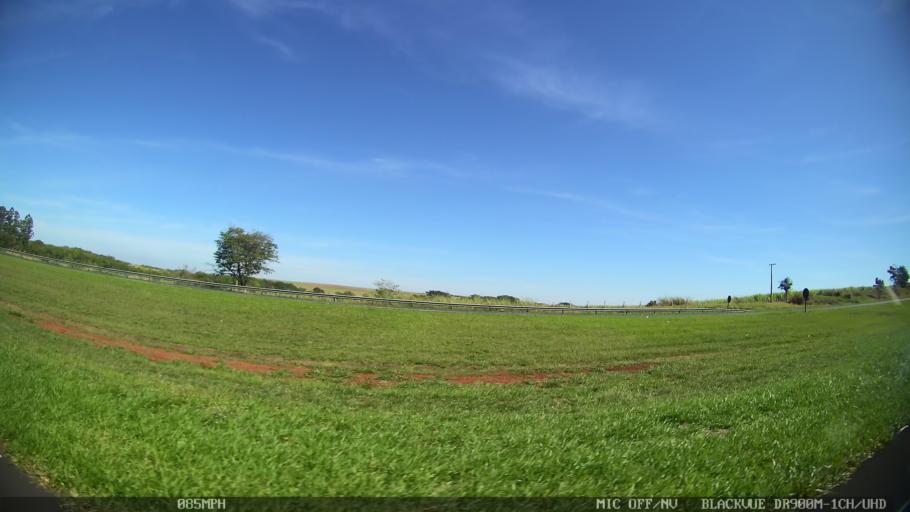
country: BR
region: Sao Paulo
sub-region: Santa Rita Do Passa Quatro
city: Santa Rita do Passa Quatro
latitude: -21.6748
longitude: -47.6054
